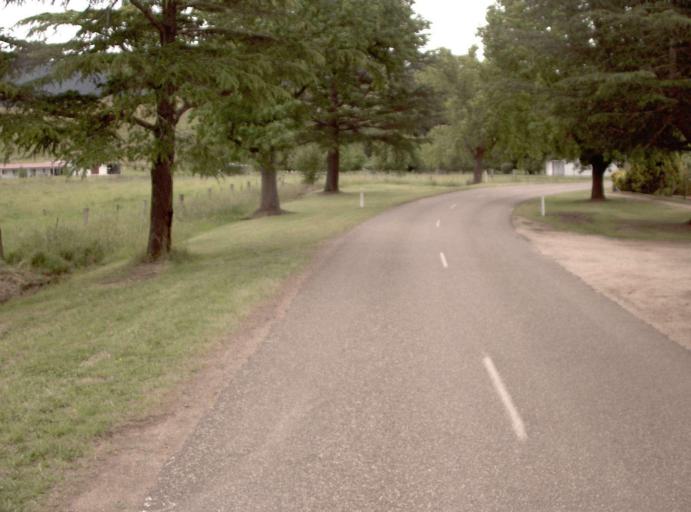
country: AU
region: Victoria
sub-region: East Gippsland
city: Bairnsdale
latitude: -37.4648
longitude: 147.2506
